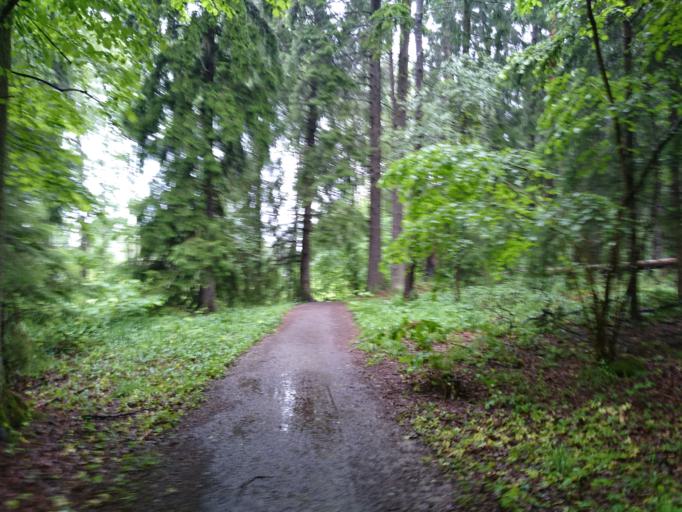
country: SE
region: Stockholm
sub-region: Huddinge Kommun
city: Segeltorp
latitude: 59.2706
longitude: 17.9316
